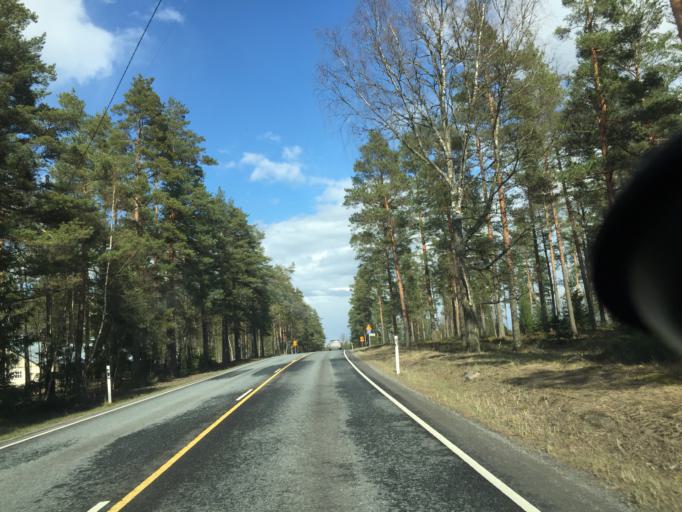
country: FI
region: Uusimaa
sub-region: Raaseporin
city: Karis
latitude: 60.1115
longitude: 23.7948
